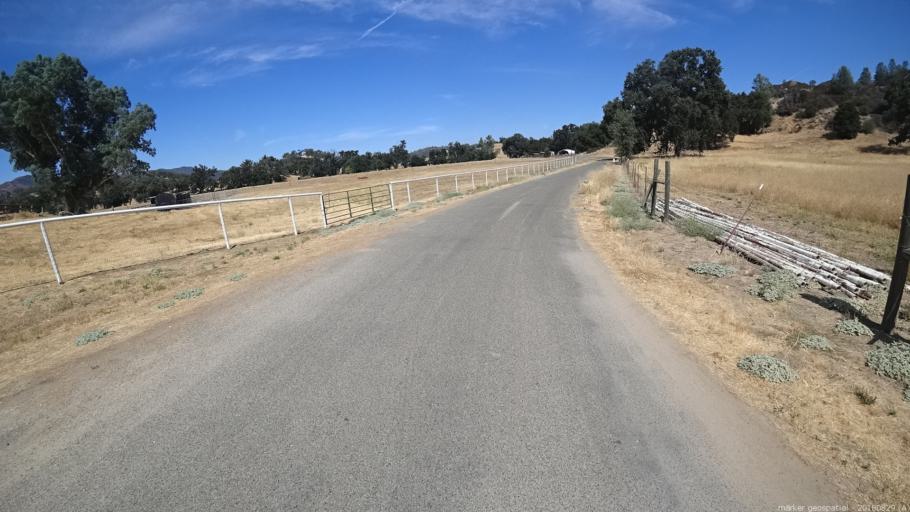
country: US
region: California
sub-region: San Luis Obispo County
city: Lake Nacimiento
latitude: 35.8120
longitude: -121.0895
